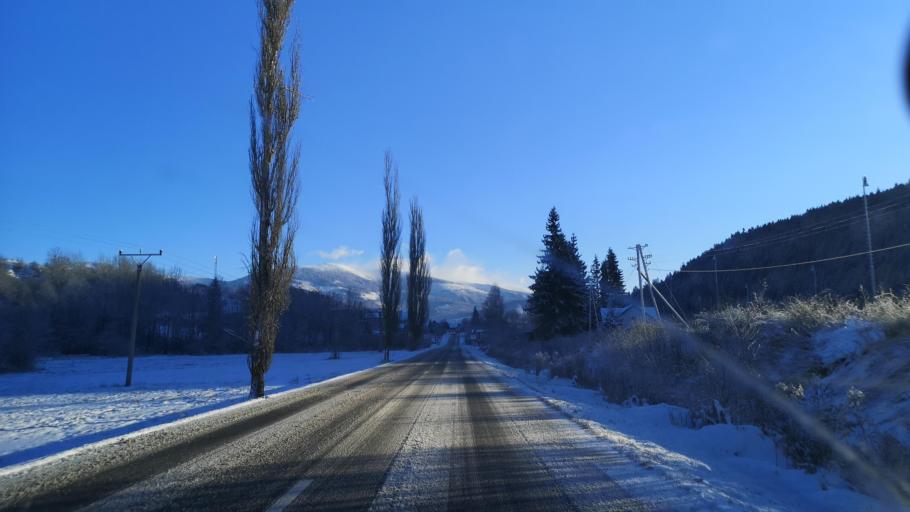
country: SK
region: Banskobystricky
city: Tisovec
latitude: 48.8565
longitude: 19.9570
